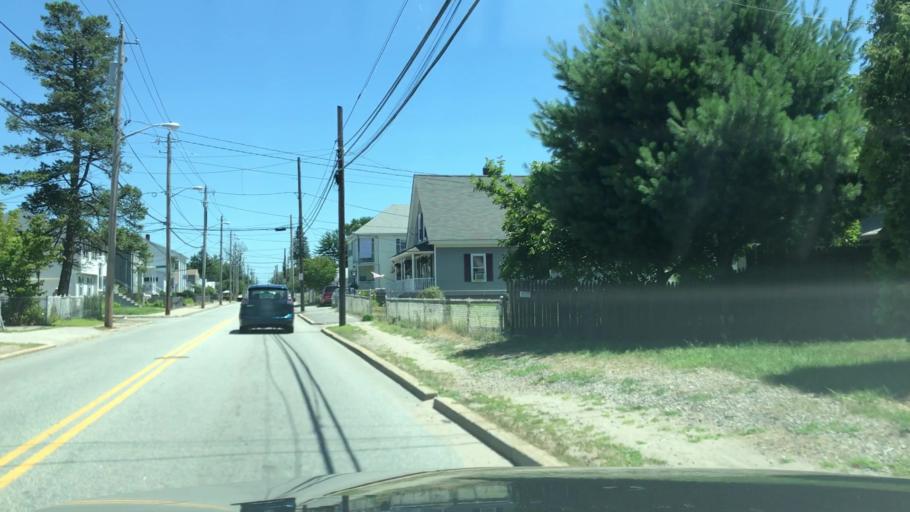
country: US
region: Rhode Island
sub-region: Providence County
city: Pawtucket
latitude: 41.8608
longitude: -71.3627
